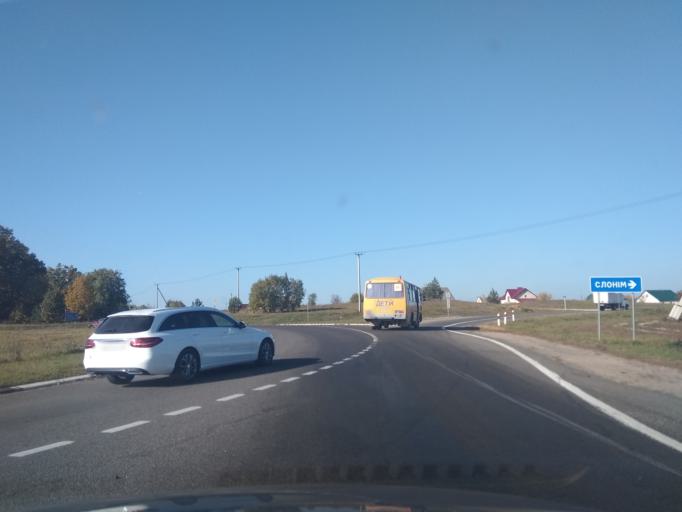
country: BY
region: Grodnenskaya
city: Slonim
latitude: 53.0578
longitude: 25.3030
